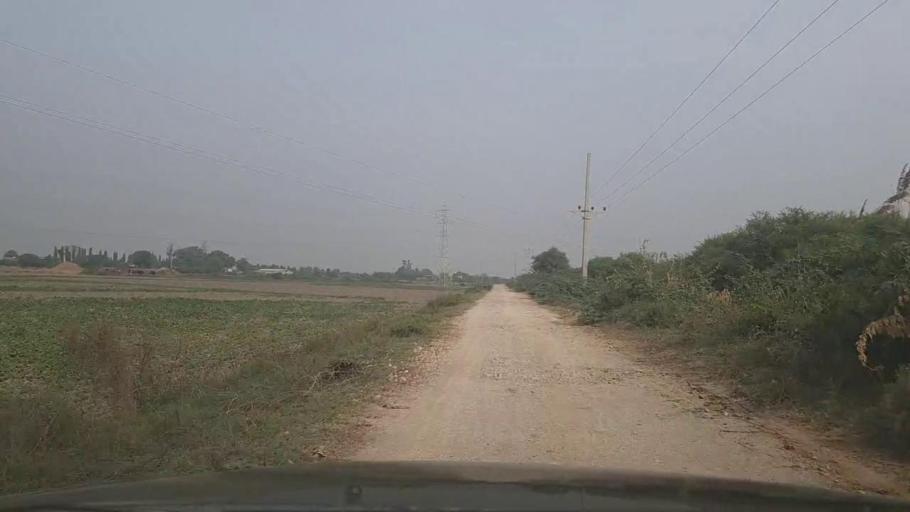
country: PK
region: Sindh
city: Mirpur Sakro
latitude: 24.5710
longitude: 67.7906
